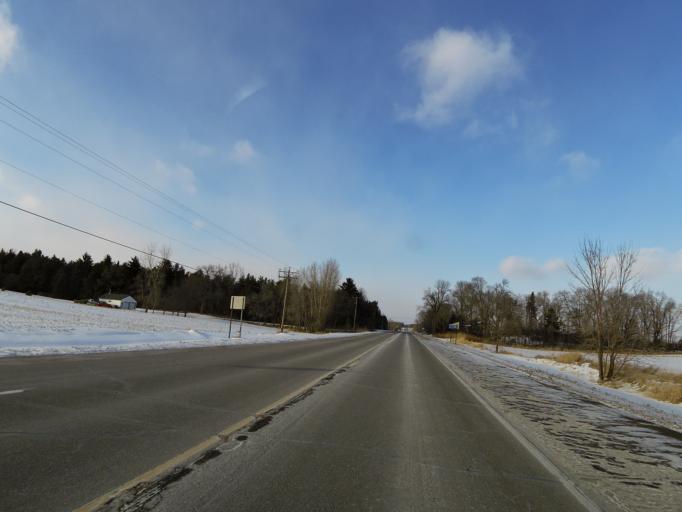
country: US
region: Minnesota
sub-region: Washington County
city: Lake Elmo
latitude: 44.9512
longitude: -92.8831
